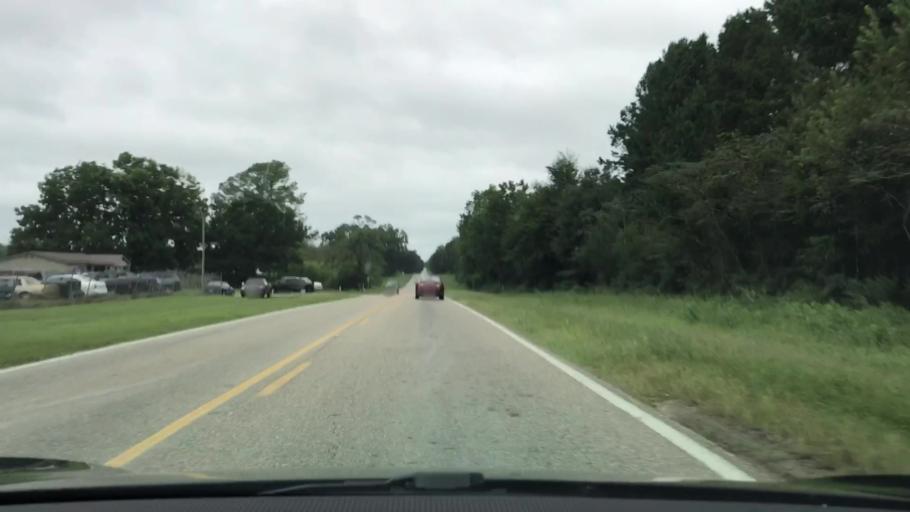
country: US
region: Alabama
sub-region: Geneva County
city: Samson
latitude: 31.1839
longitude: -86.1489
